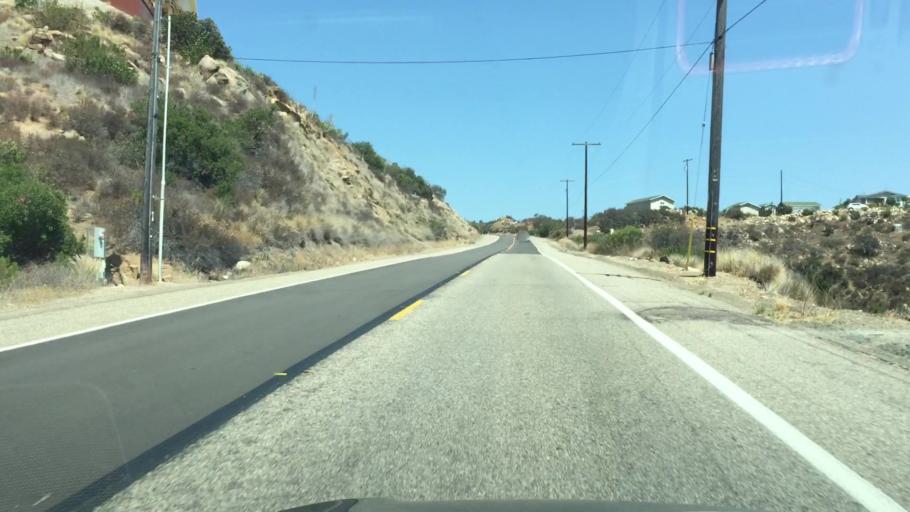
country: US
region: California
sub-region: San Diego County
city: Jamul
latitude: 32.7350
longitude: -116.8412
